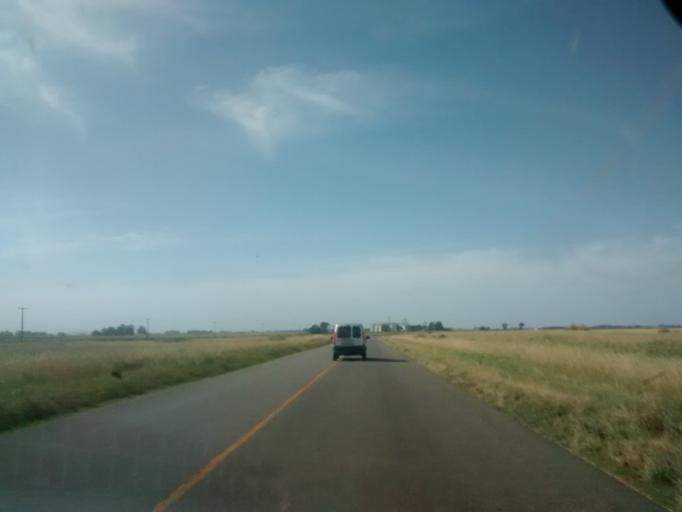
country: AR
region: Buenos Aires
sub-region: Partido de Tandil
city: Tandil
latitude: -37.5978
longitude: -58.7513
